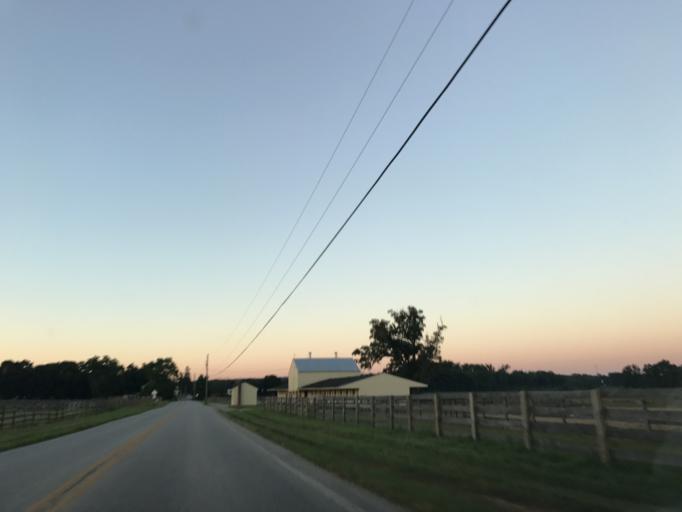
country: US
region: Pennsylvania
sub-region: Adams County
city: McSherrystown
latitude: 39.7828
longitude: -77.0297
